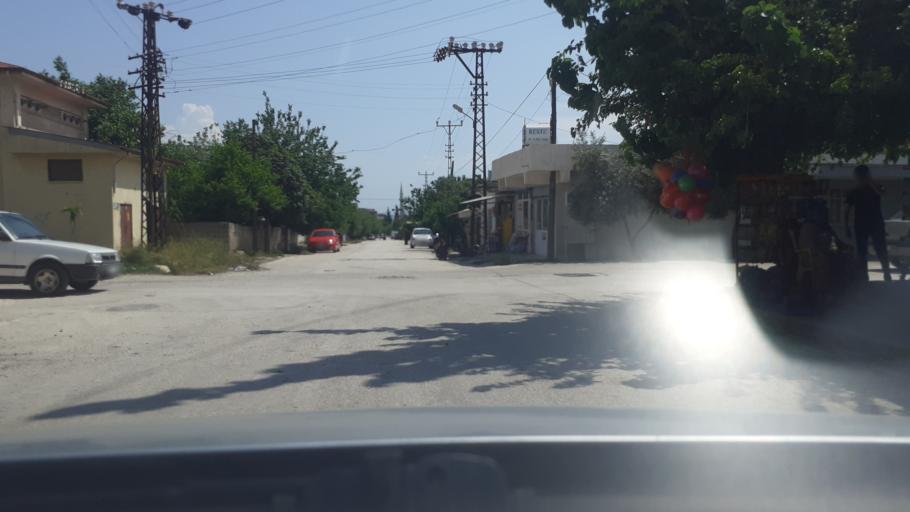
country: TR
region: Hatay
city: Kirikhan
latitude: 36.4908
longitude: 36.3540
